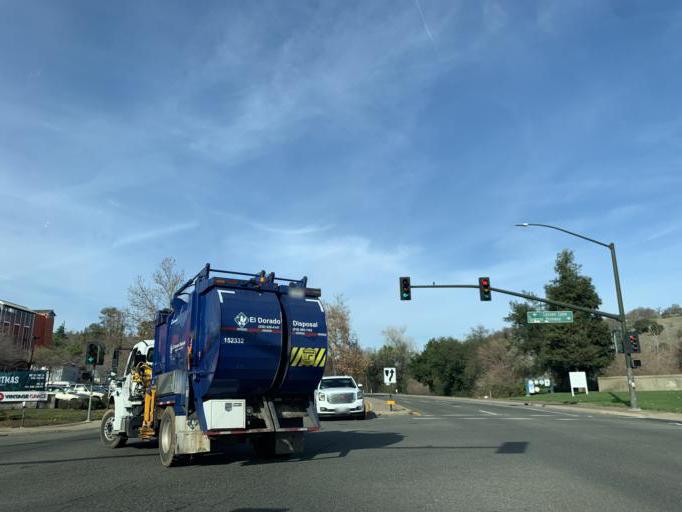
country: US
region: California
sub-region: El Dorado County
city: El Dorado Hills
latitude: 38.6601
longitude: -121.0719
